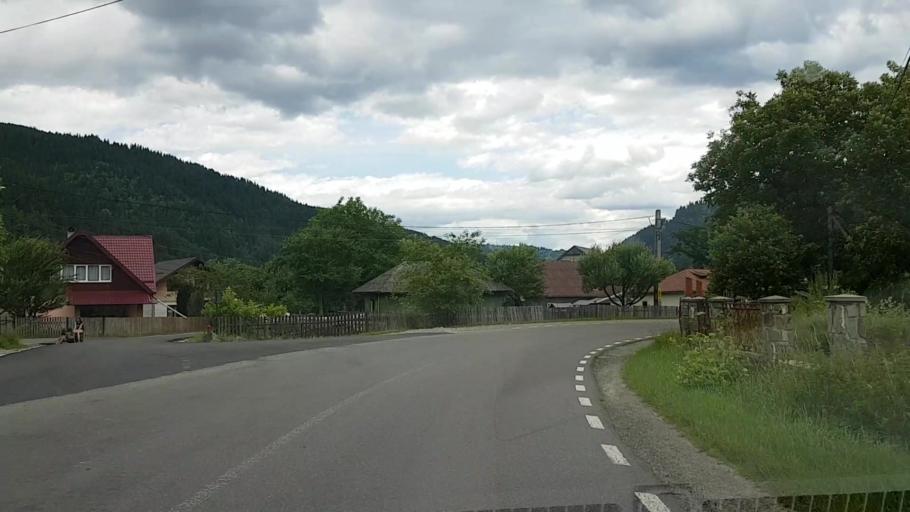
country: RO
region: Neamt
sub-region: Comuna Poiana Teiului
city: Poiana Teiului
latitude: 47.1115
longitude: 25.9316
